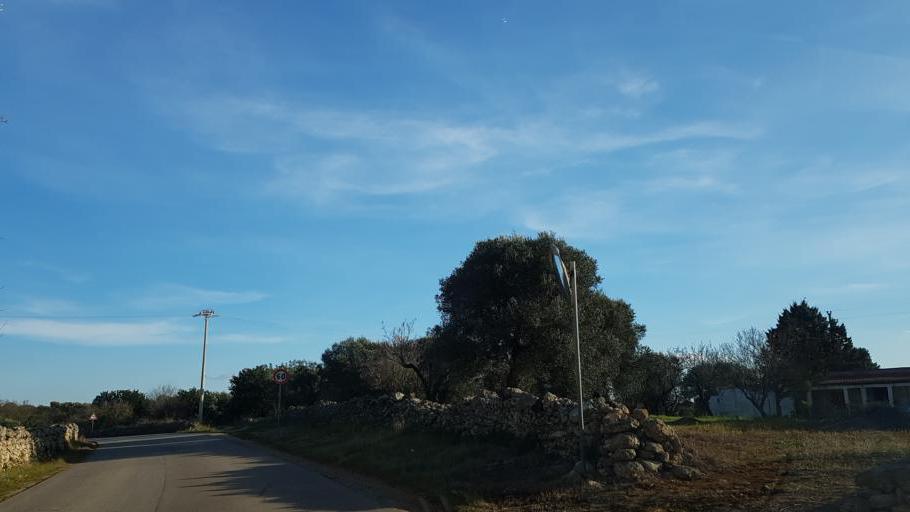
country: IT
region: Apulia
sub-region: Provincia di Brindisi
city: San Vito dei Normanni
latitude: 40.7018
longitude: 17.7268
